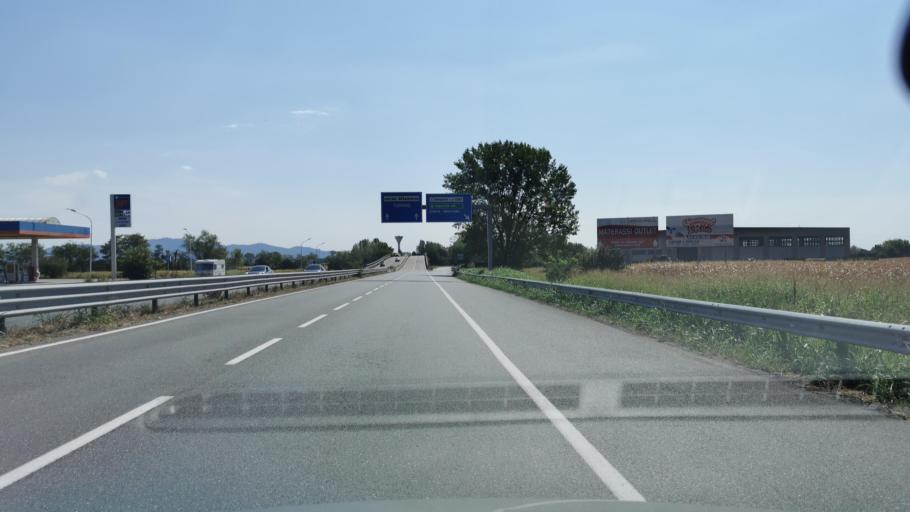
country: IT
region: Piedmont
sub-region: Provincia di Torino
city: Tetti Neirotti
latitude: 45.0559
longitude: 7.5621
